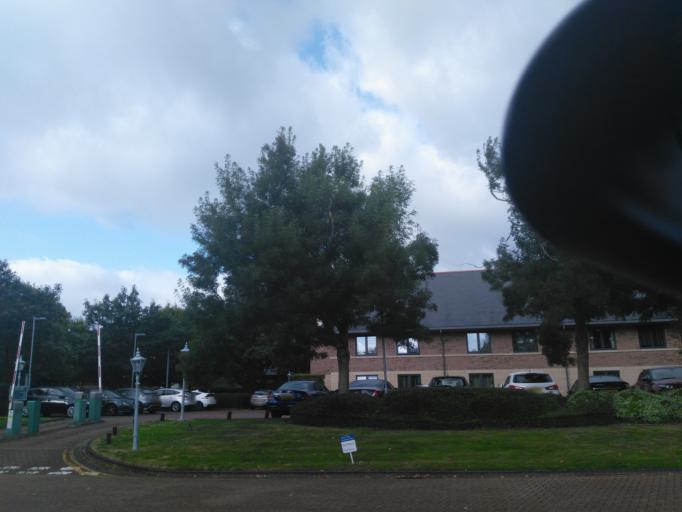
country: GB
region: England
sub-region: South Gloucestershire
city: Almondsbury
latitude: 51.5419
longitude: -2.5680
